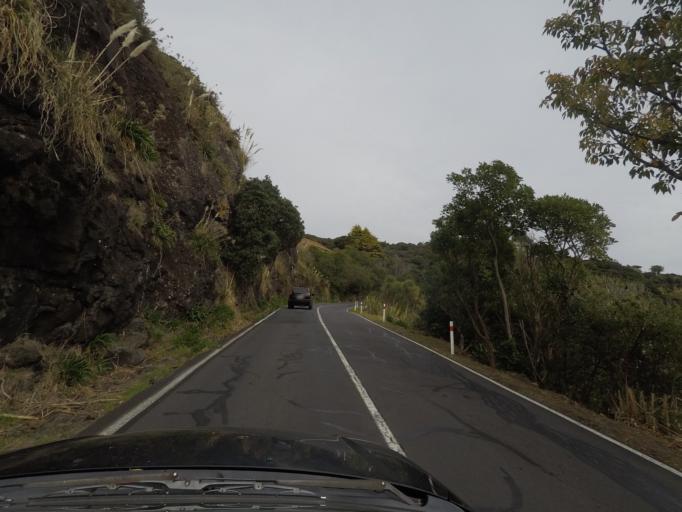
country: NZ
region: Auckland
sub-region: Auckland
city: Muriwai Beach
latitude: -36.9602
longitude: 174.4774
